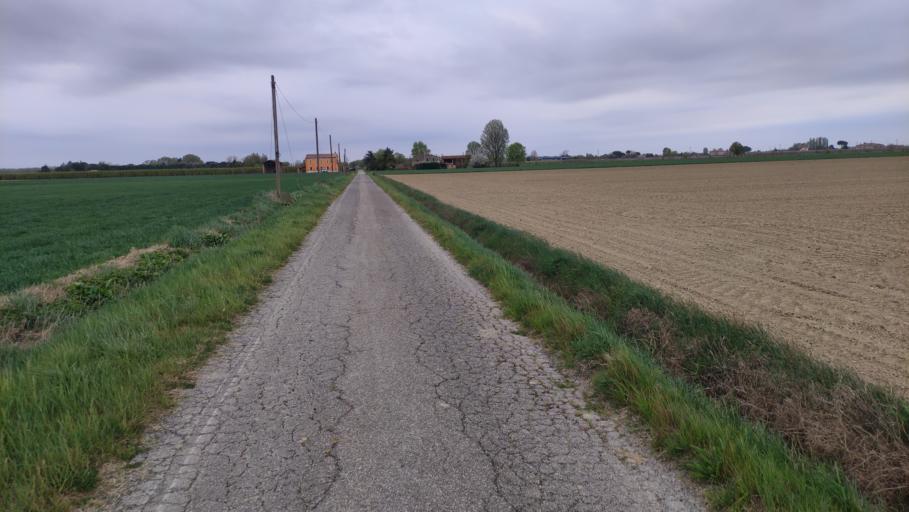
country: IT
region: Emilia-Romagna
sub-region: Provincia di Ravenna
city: Russi
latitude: 44.3972
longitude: 12.0459
